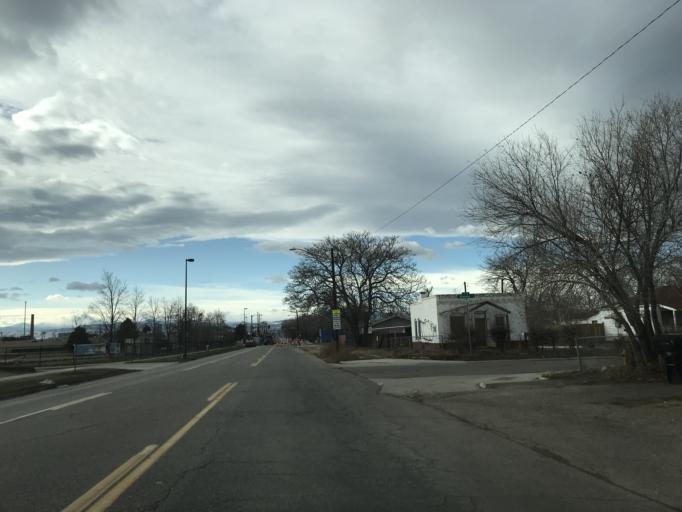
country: US
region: Colorado
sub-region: Adams County
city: Commerce City
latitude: 39.7729
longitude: -104.9515
